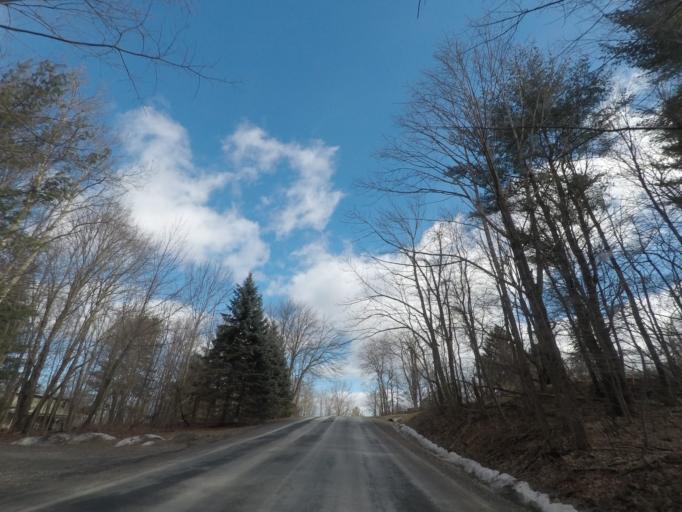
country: US
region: New York
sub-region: Rensselaer County
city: Averill Park
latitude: 42.6665
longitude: -73.5155
